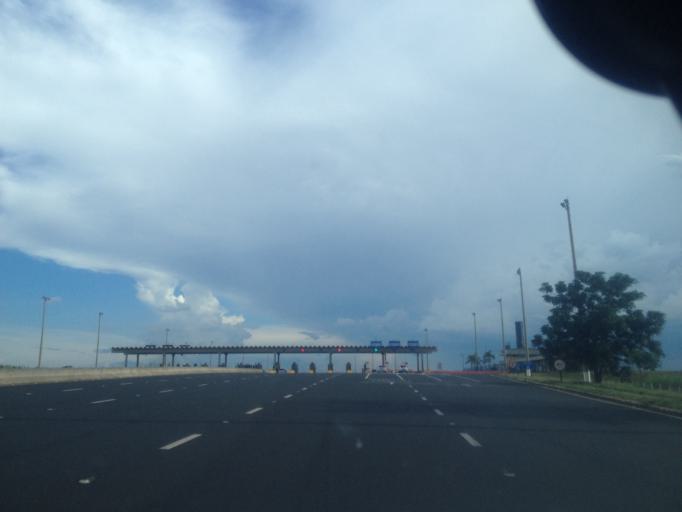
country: BR
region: Sao Paulo
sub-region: Santa Rita Do Passa Quatro
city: Santa Rita do Passa Quatro
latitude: -21.6568
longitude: -47.6094
